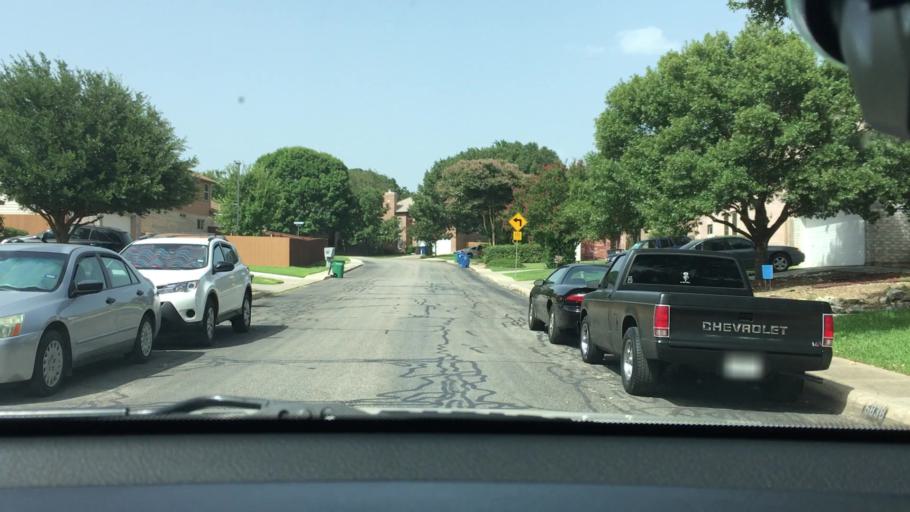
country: US
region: Texas
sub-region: Bexar County
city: Live Oak
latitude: 29.5811
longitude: -98.3832
